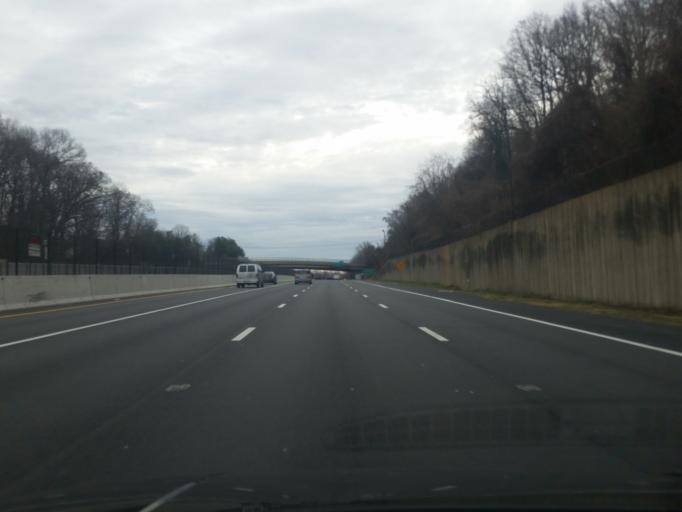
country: US
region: Virginia
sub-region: City of Falls Church
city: Falls Church
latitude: 38.8994
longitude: -77.1825
